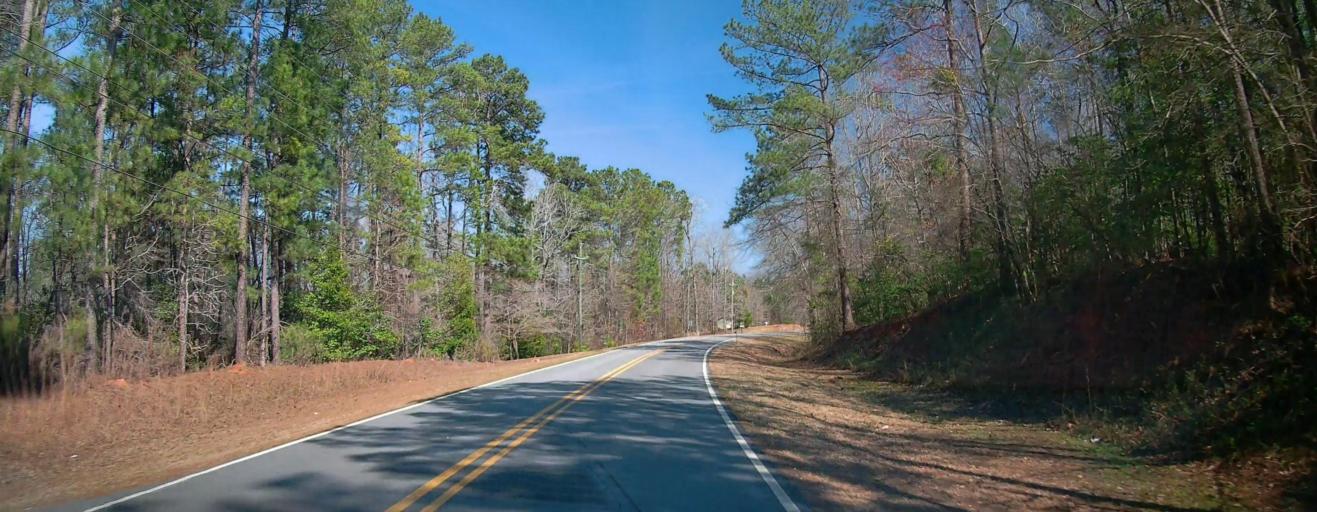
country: US
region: Georgia
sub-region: Bibb County
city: Macon
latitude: 32.9052
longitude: -83.6285
